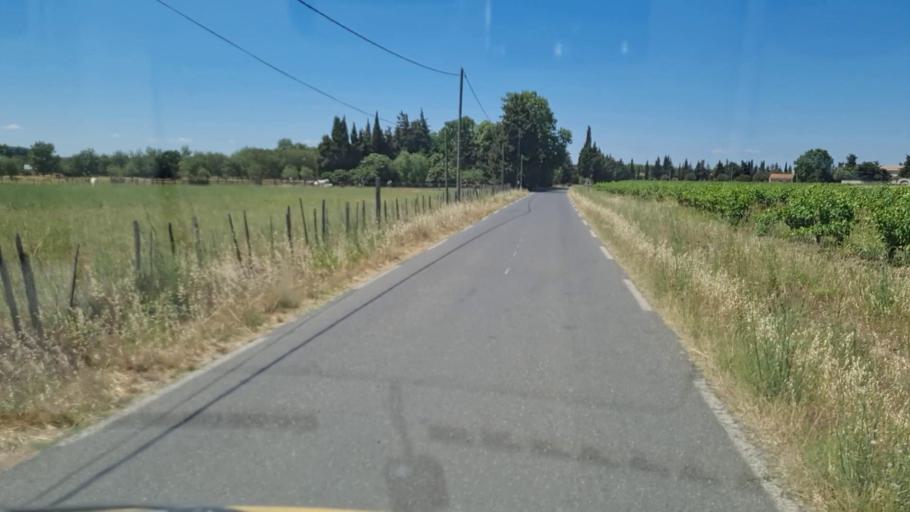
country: FR
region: Languedoc-Roussillon
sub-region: Departement du Gard
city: Le Cailar
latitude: 43.6693
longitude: 4.2588
